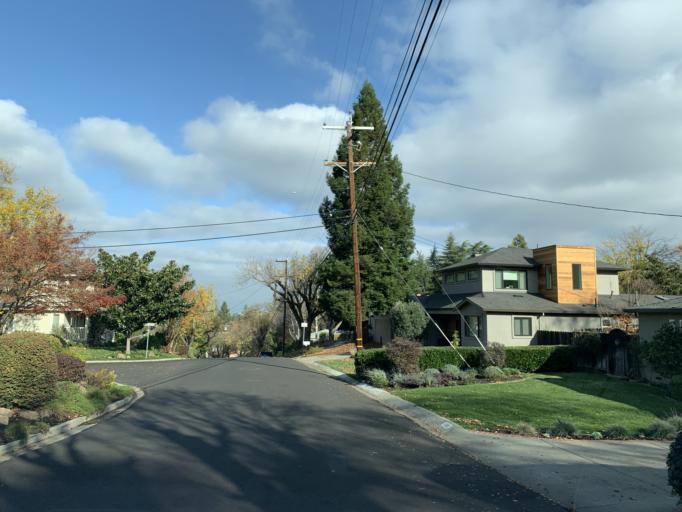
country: US
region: California
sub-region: Contra Costa County
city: Saranap
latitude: 37.8845
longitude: -122.0682
